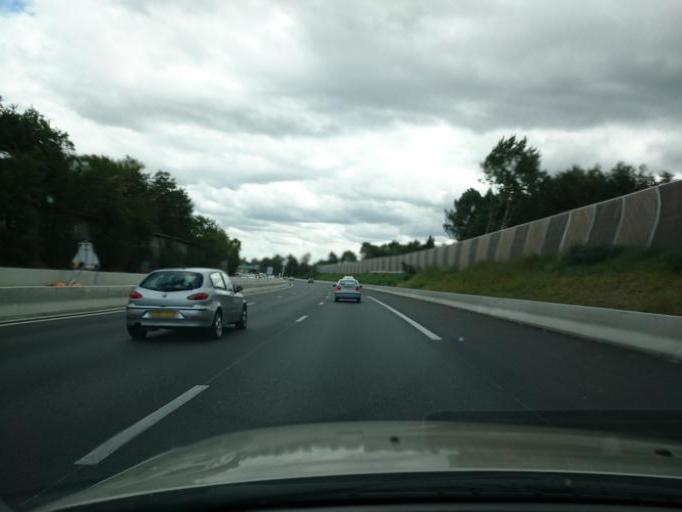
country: FR
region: Aquitaine
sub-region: Departement de la Gironde
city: Pessac
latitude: 44.8097
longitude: -0.6707
